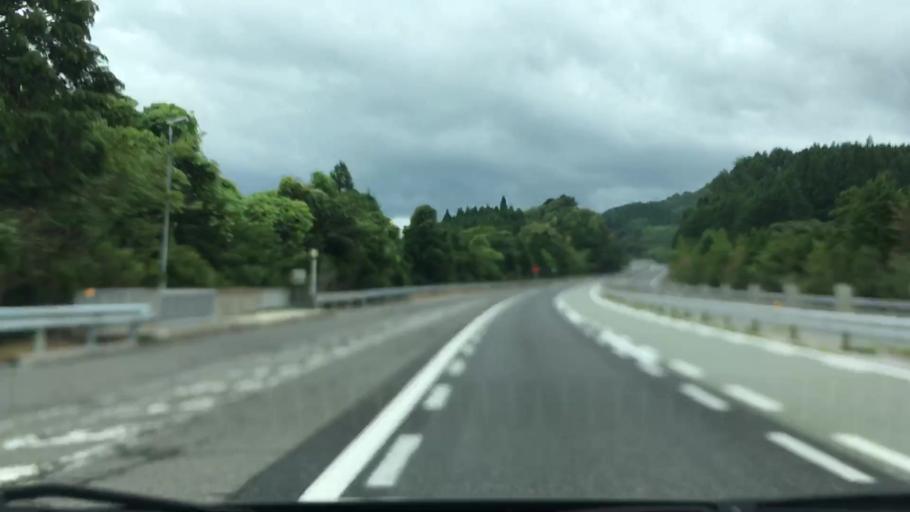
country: JP
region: Okayama
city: Niimi
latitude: 34.9460
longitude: 133.3298
